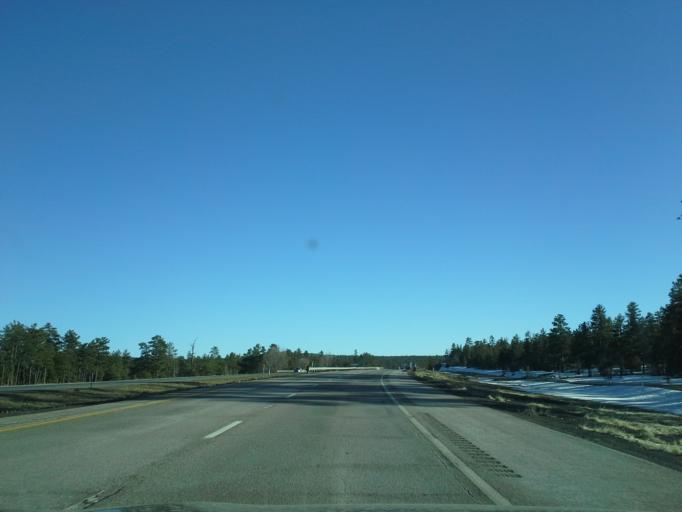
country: US
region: Arizona
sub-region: Coconino County
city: Sedona
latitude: 34.8551
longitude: -111.6083
